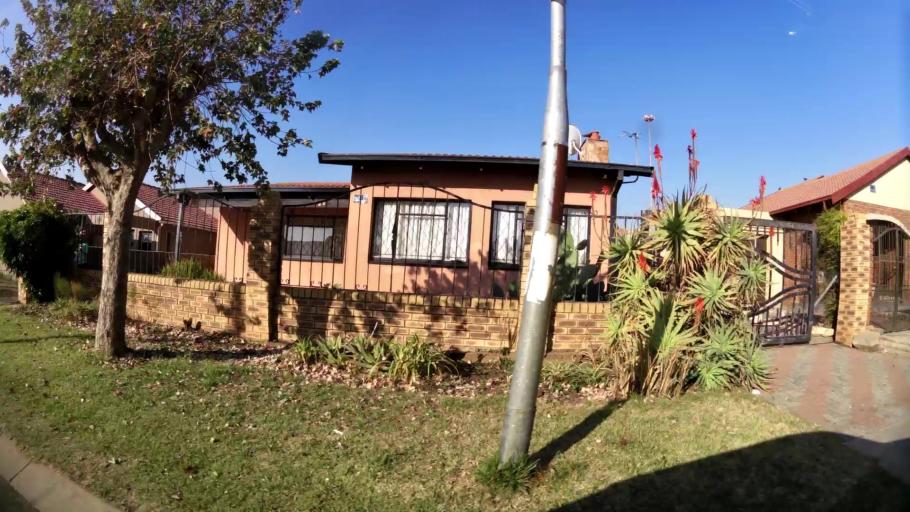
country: ZA
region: Gauteng
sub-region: City of Johannesburg Metropolitan Municipality
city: Soweto
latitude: -26.2672
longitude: 27.8694
